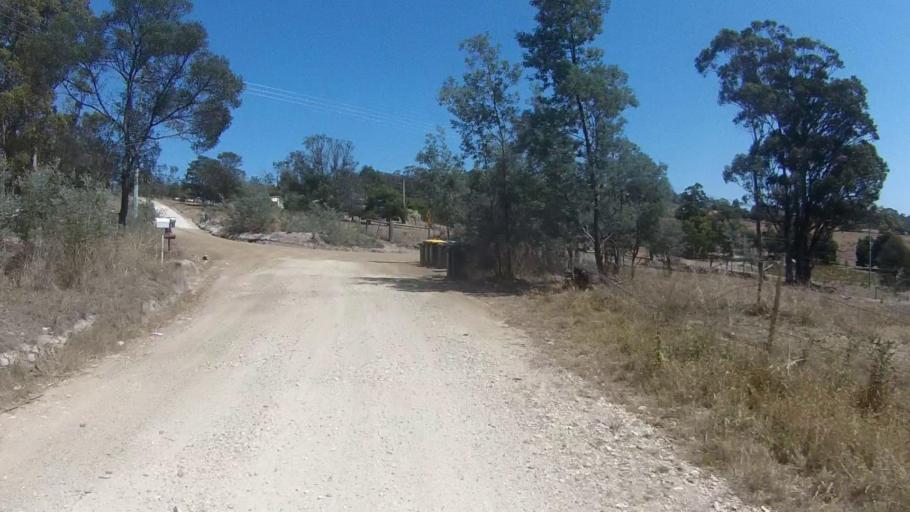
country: AU
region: Tasmania
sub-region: Sorell
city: Sorell
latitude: -42.8285
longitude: 147.6567
